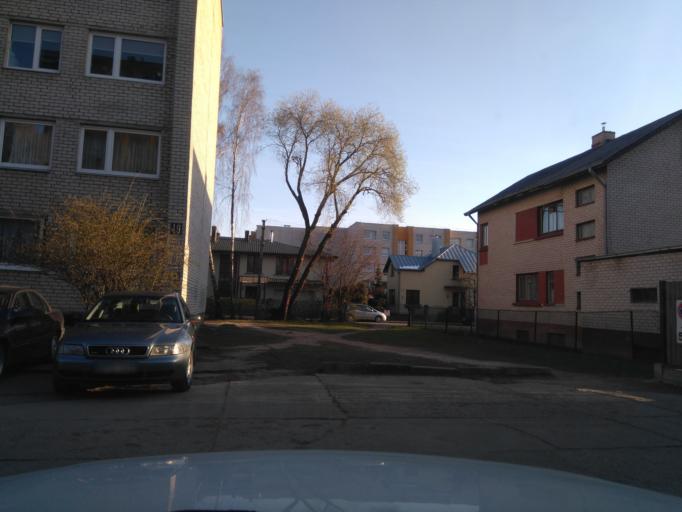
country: LT
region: Kauno apskritis
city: Dainava (Kaunas)
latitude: 54.9114
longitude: 23.9612
